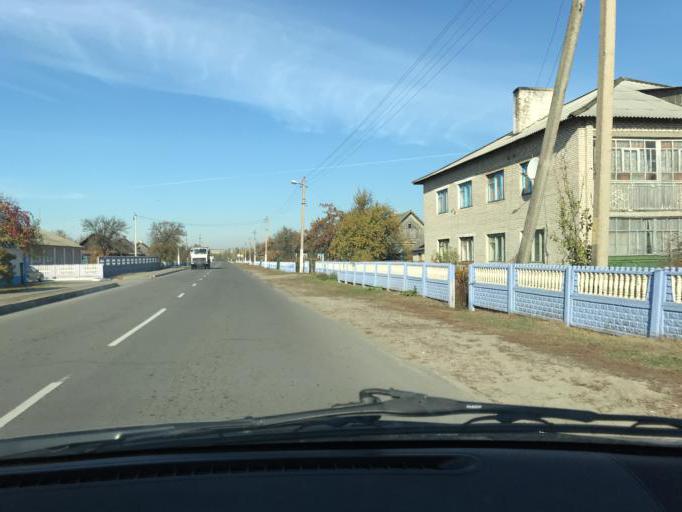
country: BY
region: Brest
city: Mikashevichy
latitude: 52.2293
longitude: 27.4564
